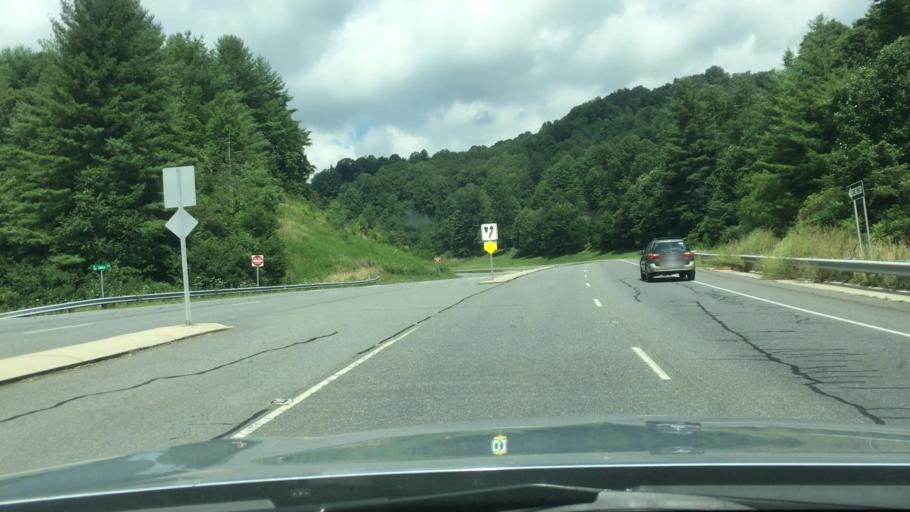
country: US
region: North Carolina
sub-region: Madison County
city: Mars Hill
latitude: 35.9129
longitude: -82.4471
